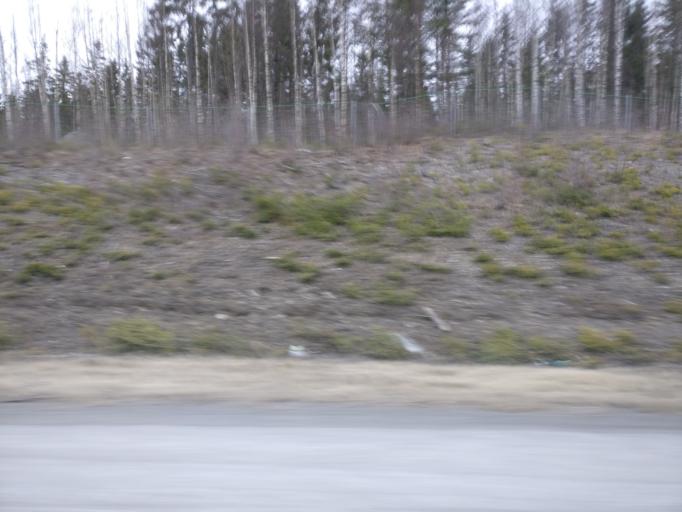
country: FI
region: Pirkanmaa
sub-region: Tampere
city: Lempaeaelae
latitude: 61.2993
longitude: 23.8208
